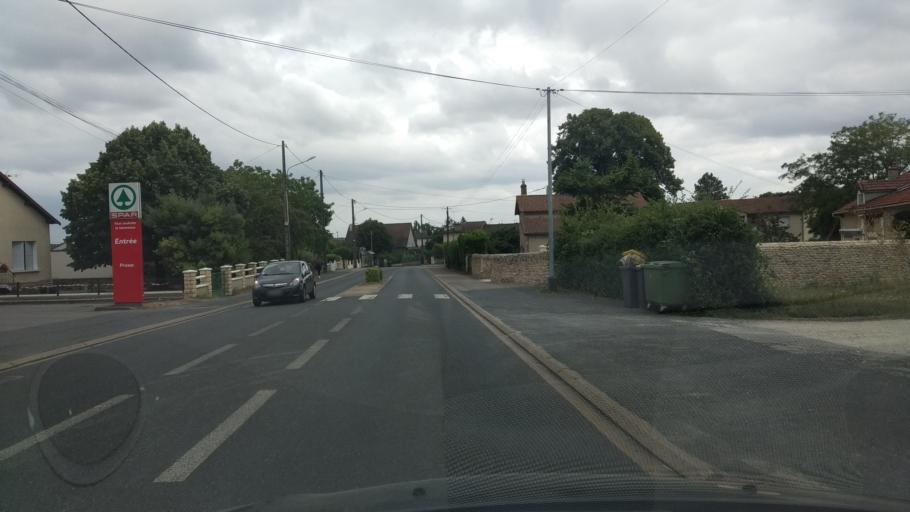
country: FR
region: Poitou-Charentes
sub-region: Departement de la Vienne
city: Roches-Premarie-Andille
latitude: 46.4862
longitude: 0.3694
